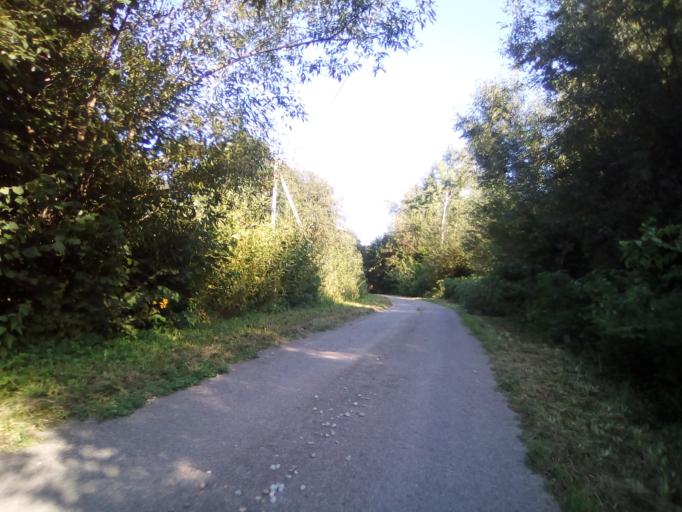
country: PL
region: Subcarpathian Voivodeship
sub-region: Powiat brzozowski
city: Domaradz
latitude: 49.8091
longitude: 21.9662
